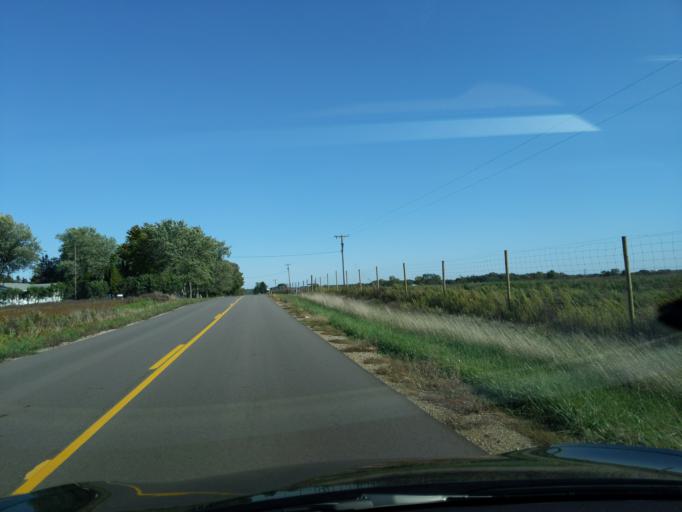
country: US
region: Michigan
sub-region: Eaton County
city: Potterville
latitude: 42.6404
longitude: -84.7938
